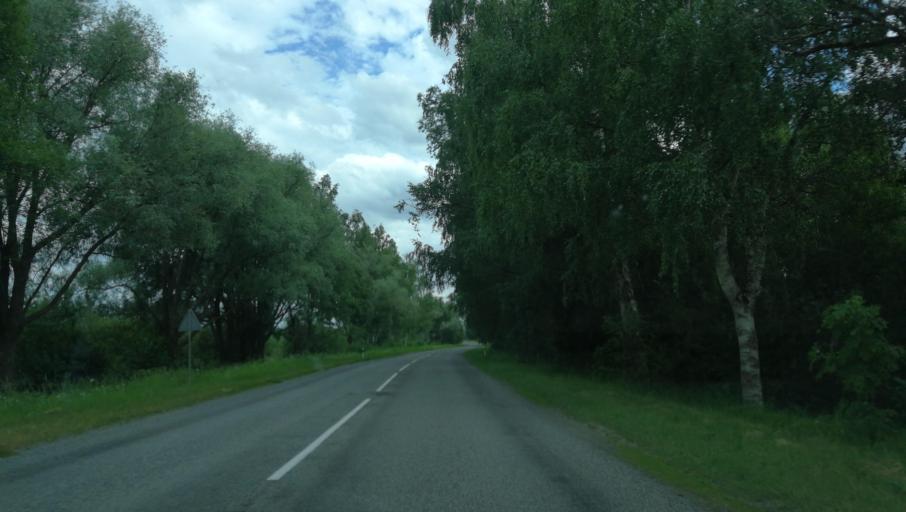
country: LV
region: Rujienas
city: Rujiena
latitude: 57.8551
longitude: 25.3770
